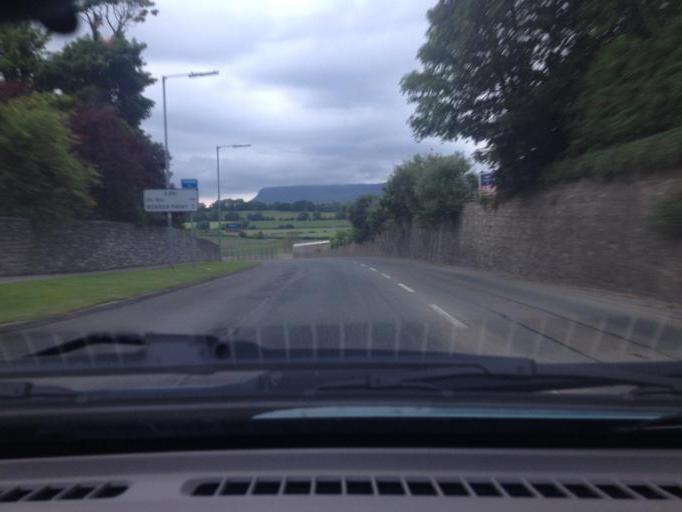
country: IE
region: Connaught
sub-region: Sligo
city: Sligo
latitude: 54.2813
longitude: -8.4752
